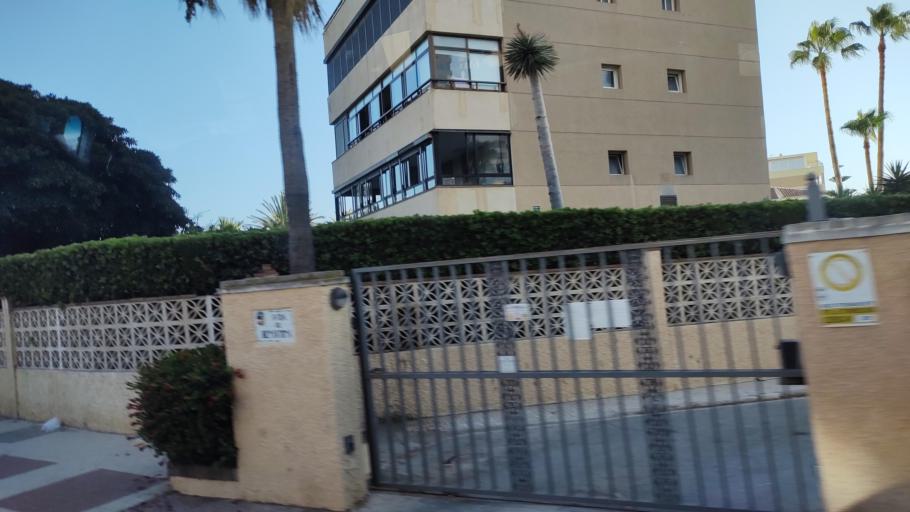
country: ES
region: Andalusia
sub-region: Provincia de Malaga
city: Torremolinos
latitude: 36.6298
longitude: -4.4904
